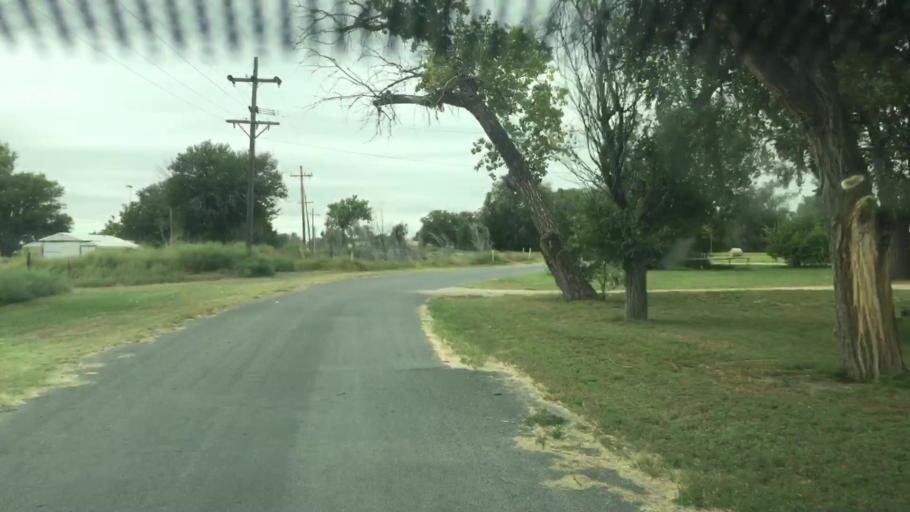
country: US
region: Kansas
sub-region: Hamilton County
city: Syracuse
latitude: 38.0571
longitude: -102.1166
